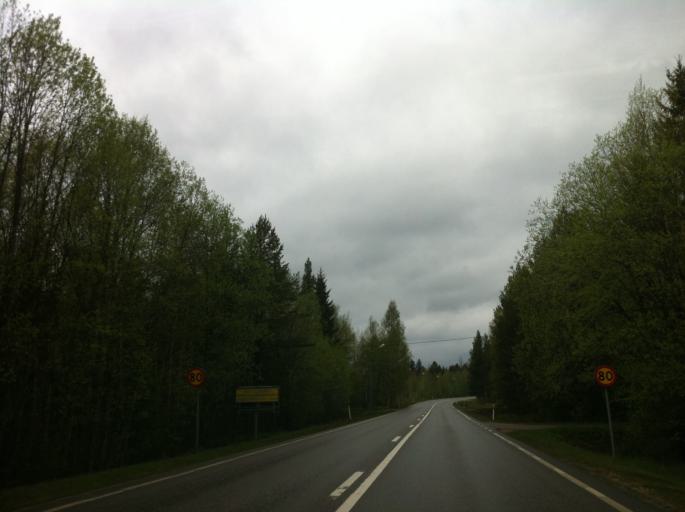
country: SE
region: Jaemtland
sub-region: Harjedalens Kommun
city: Sveg
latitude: 62.0619
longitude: 14.2828
